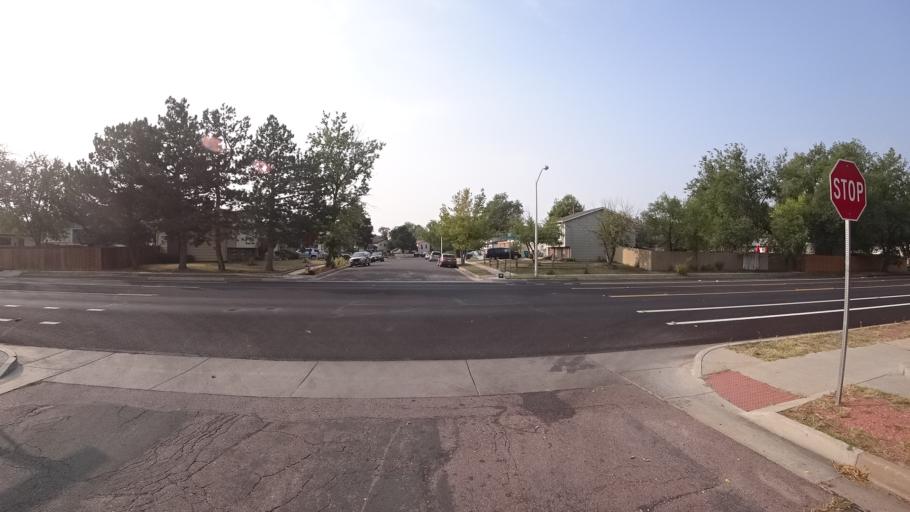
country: US
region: Colorado
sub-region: El Paso County
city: Stratmoor
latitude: 38.7969
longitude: -104.7523
